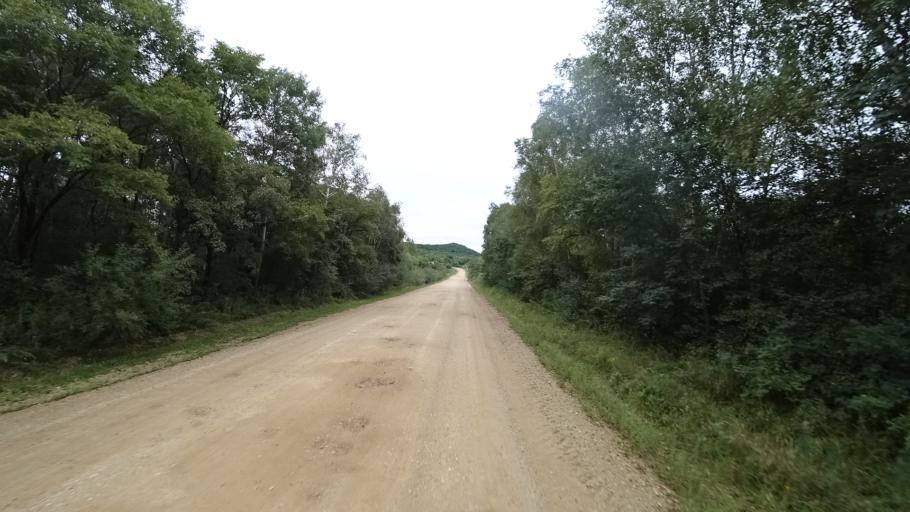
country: RU
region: Primorskiy
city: Rettikhovka
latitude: 44.1647
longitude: 132.7330
